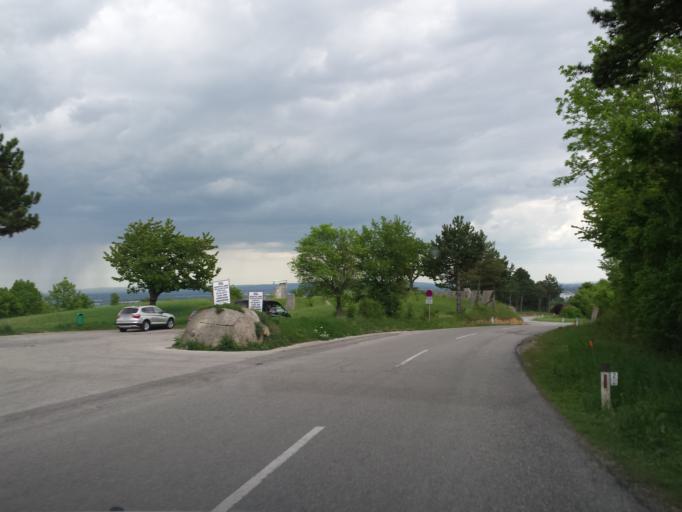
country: AT
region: Lower Austria
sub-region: Politischer Bezirk Baden
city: Hirtenberg
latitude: 47.9125
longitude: 16.1605
